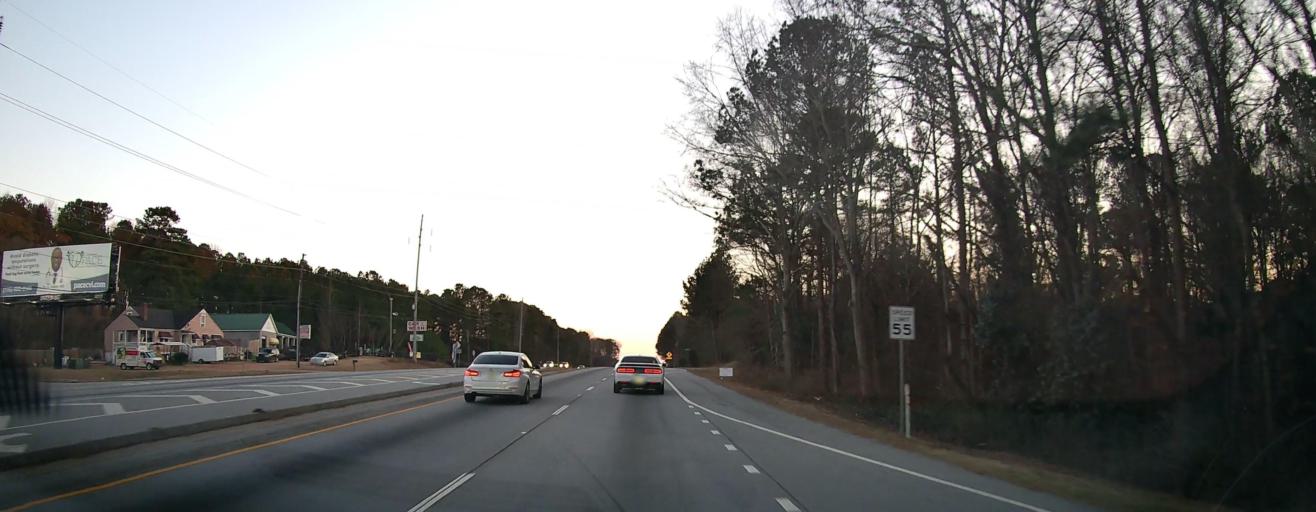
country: US
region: Georgia
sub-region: Clayton County
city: Riverdale
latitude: 33.5334
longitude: -84.4194
